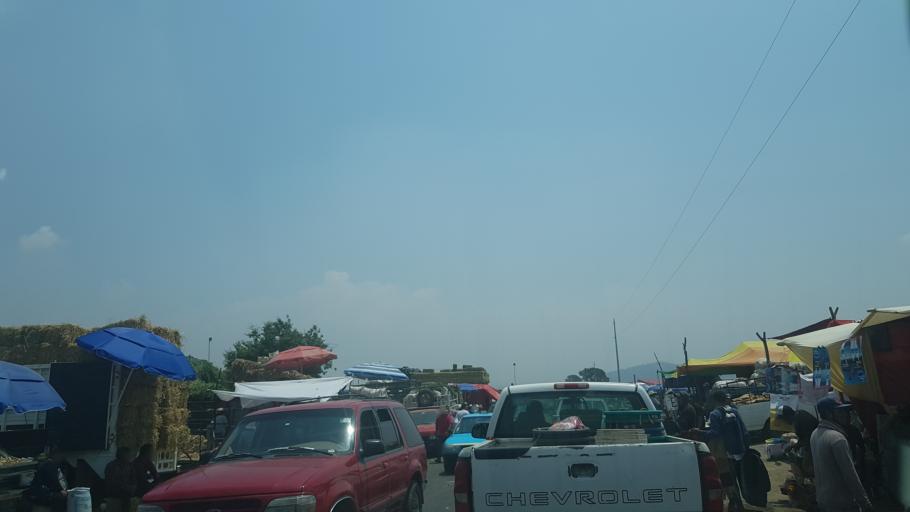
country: MX
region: Puebla
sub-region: San Jeronimo Tecuanipan
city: San Miguel Papaxtla
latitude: 19.0966
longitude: -98.4141
